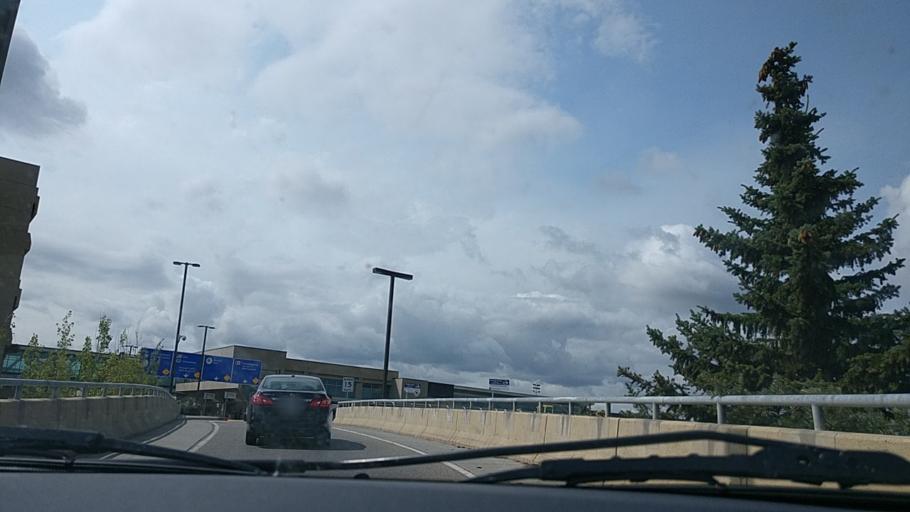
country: CA
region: Alberta
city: Calgary
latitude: 51.1340
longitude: -114.0107
